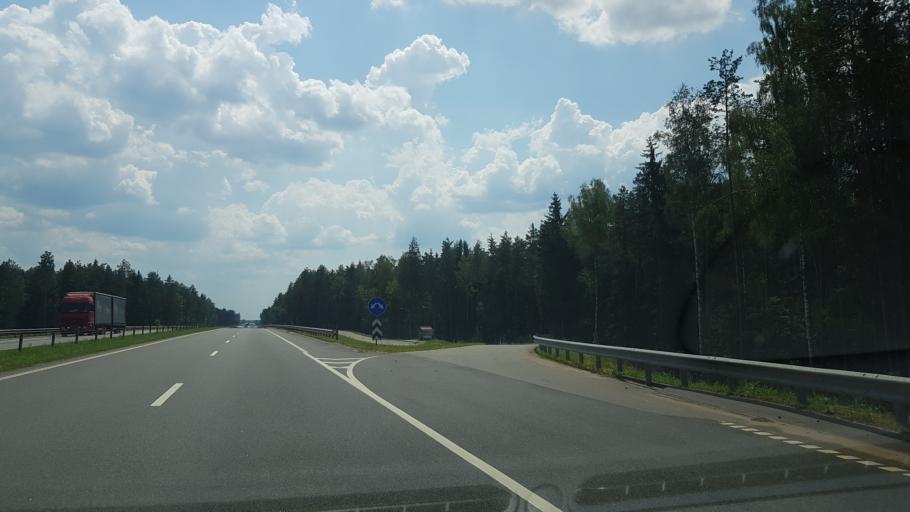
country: BY
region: Mogilev
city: Babruysk
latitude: 53.2125
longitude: 29.3438
